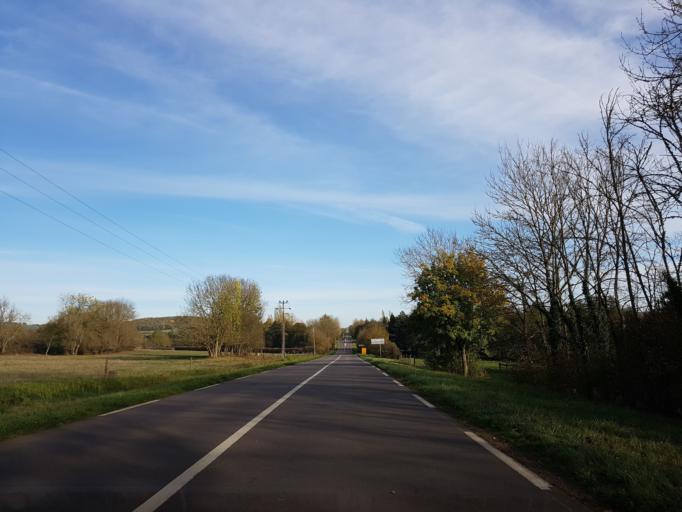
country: FR
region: Bourgogne
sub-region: Departement de la Cote-d'Or
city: Vitteaux
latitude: 47.3929
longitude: 4.4290
